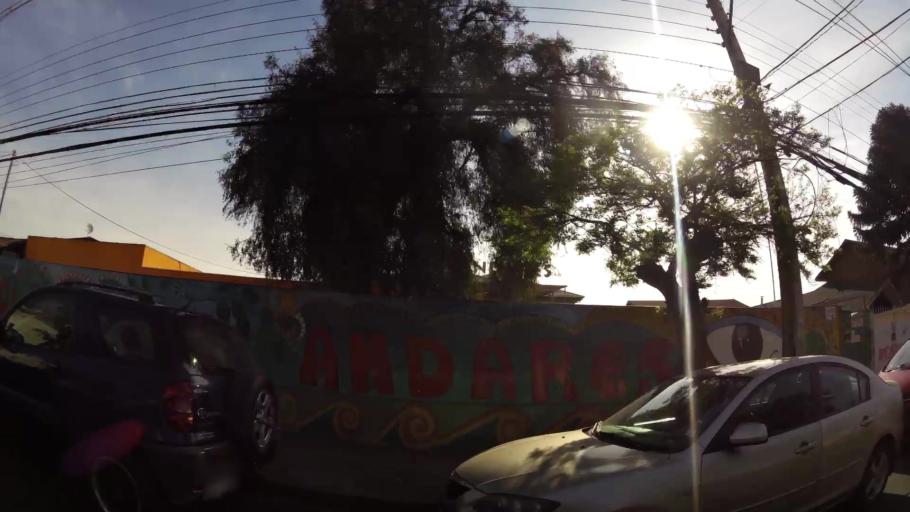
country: CL
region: Santiago Metropolitan
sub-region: Provincia de Santiago
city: Villa Presidente Frei, Nunoa, Santiago, Chile
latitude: -33.5231
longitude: -70.5840
